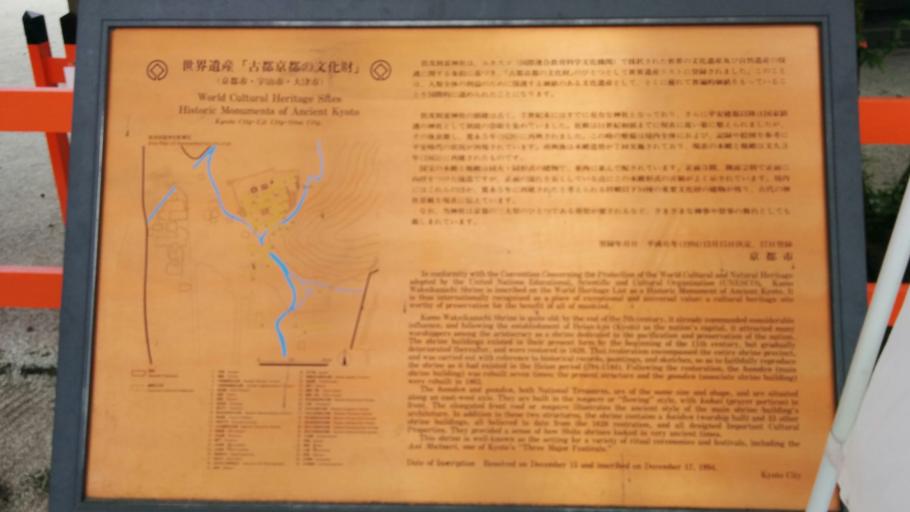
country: JP
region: Kyoto
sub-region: Kyoto-shi
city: Kamigyo-ku
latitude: 35.0595
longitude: 135.7525
